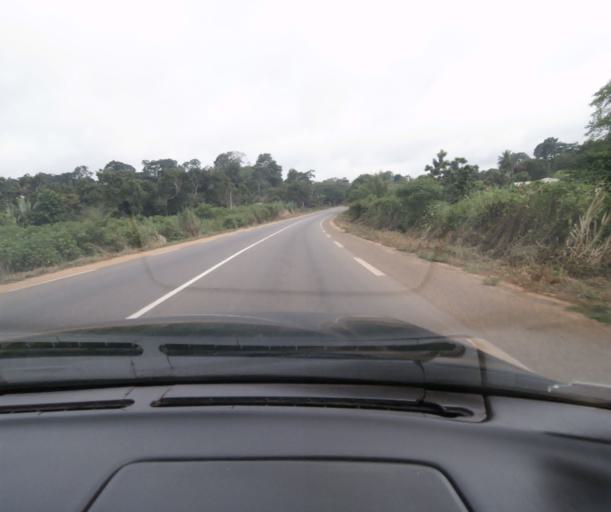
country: CM
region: Centre
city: Obala
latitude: 4.1109
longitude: 11.5279
